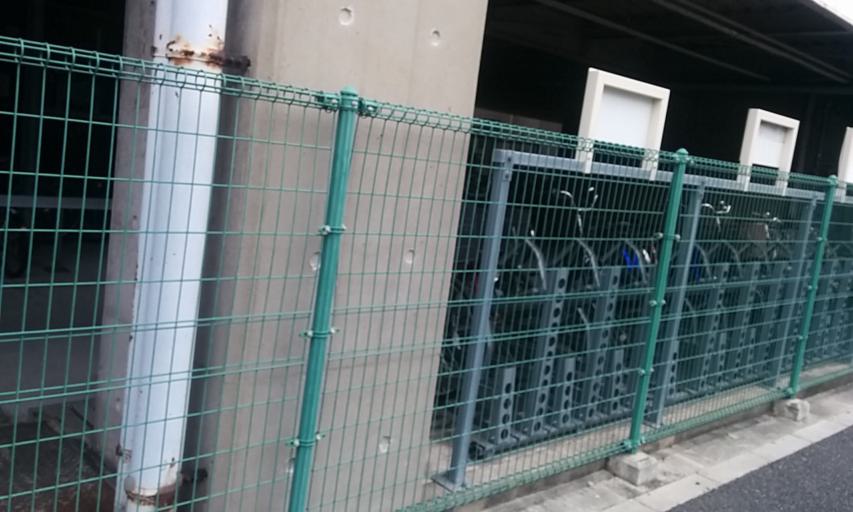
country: JP
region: Osaka
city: Yao
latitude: 34.6570
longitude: 135.5726
